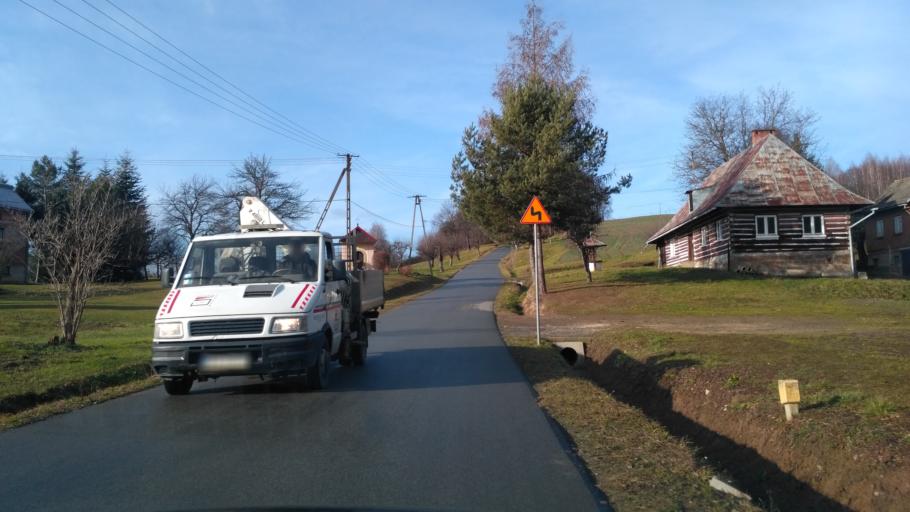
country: PL
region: Subcarpathian Voivodeship
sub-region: Powiat krosnienski
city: Korczyna
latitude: 49.7242
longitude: 21.8006
